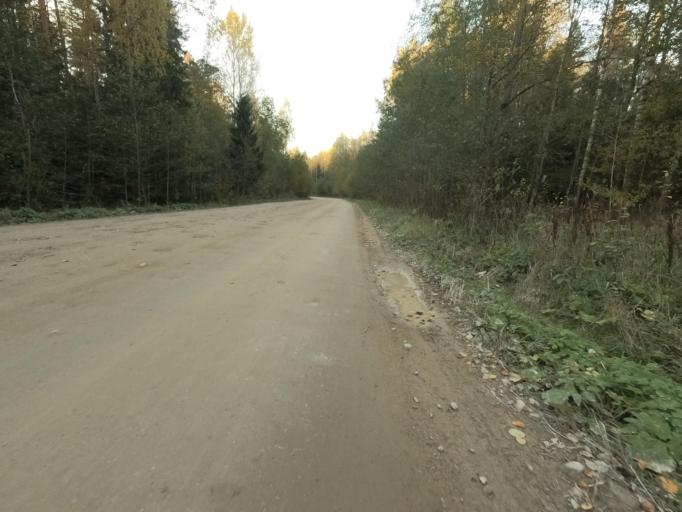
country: RU
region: Leningrad
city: Lyuban'
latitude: 59.0133
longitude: 31.0881
